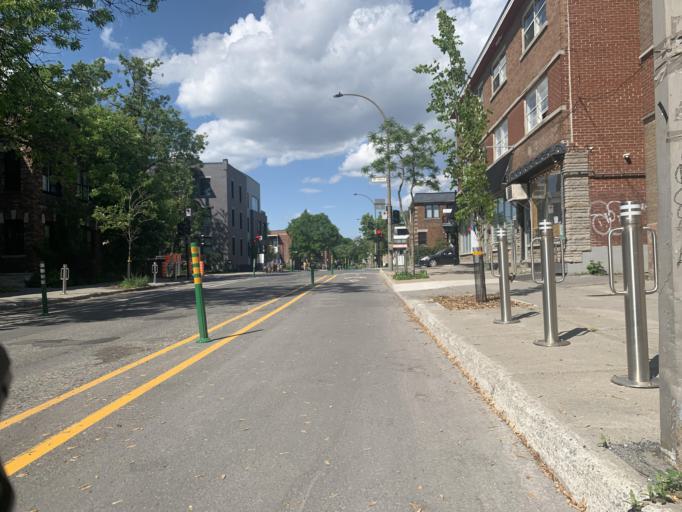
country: CA
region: Quebec
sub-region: Montreal
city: Saint-Leonard
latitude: 45.5491
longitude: -73.5866
